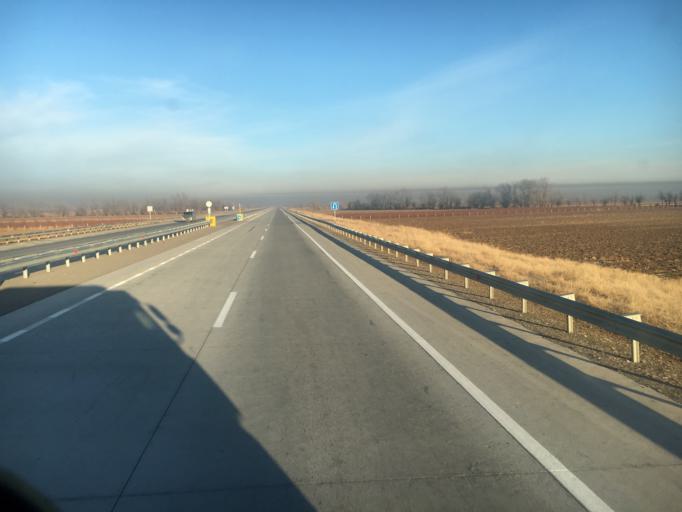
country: KZ
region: Ongtustik Qazaqstan
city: Turkestan
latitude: 43.1834
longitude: 68.4973
